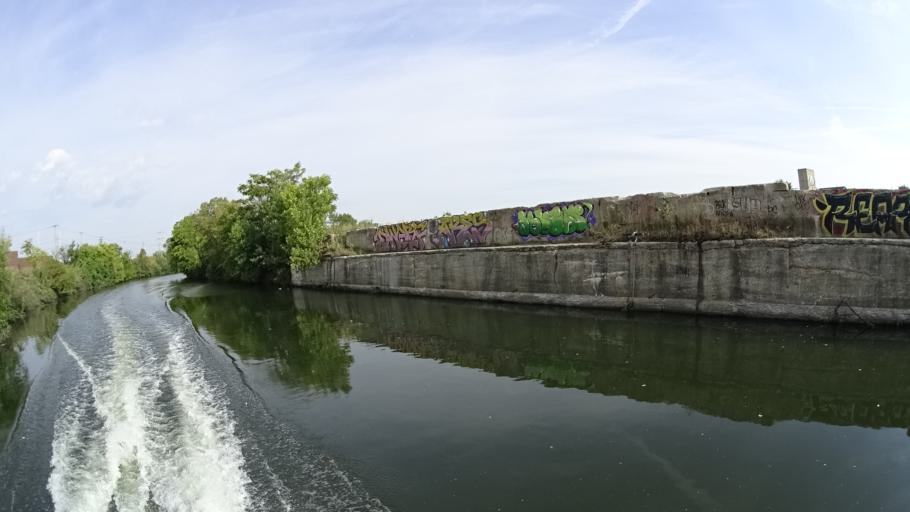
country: US
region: Illinois
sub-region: Cook County
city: Chicago
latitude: 41.8357
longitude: -87.6620
